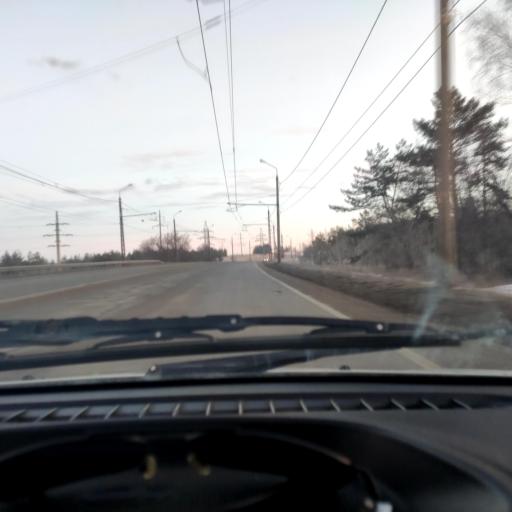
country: RU
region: Samara
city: Zhigulevsk
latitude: 53.5064
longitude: 49.5176
